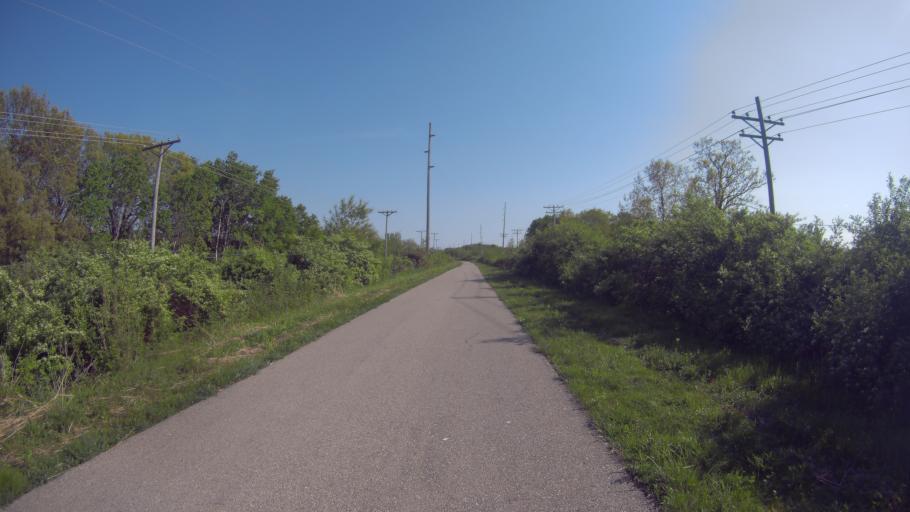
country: US
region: Wisconsin
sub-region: Dane County
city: Shorewood Hills
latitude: 43.0227
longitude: -89.4613
